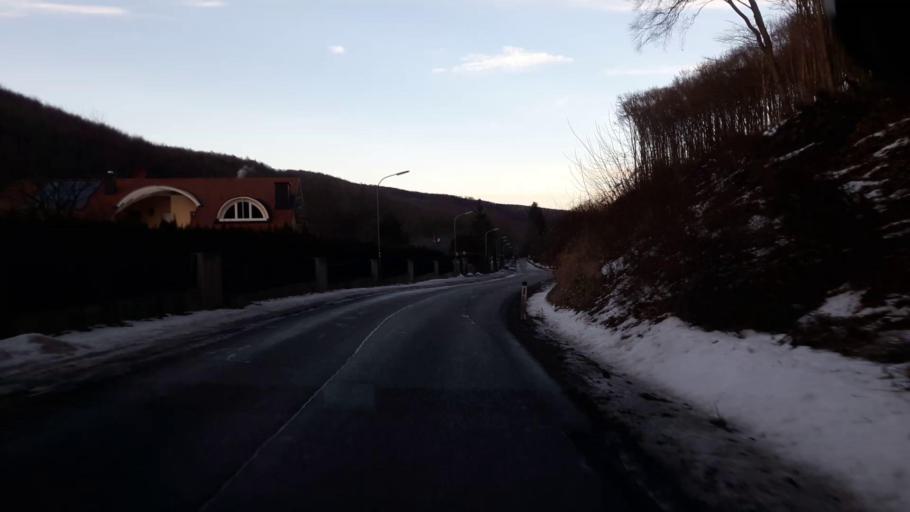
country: AT
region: Lower Austria
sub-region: Politischer Bezirk Wien-Umgebung
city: Klosterneuburg
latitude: 48.2683
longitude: 16.2728
